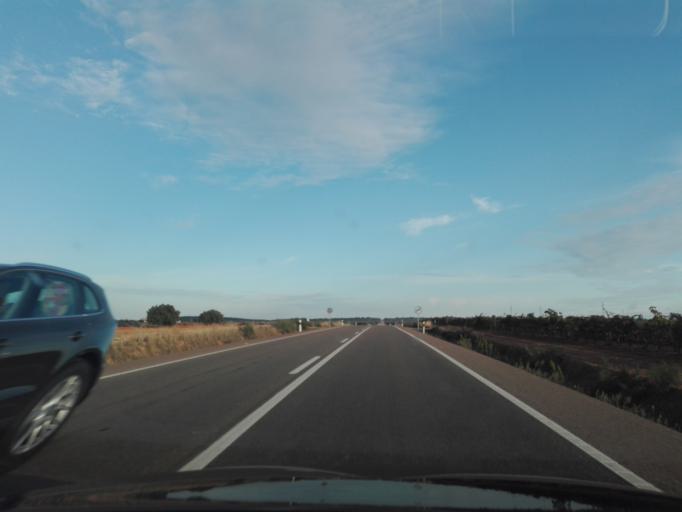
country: ES
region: Extremadura
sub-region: Provincia de Badajoz
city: Bienvenida
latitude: 38.3767
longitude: -6.2645
